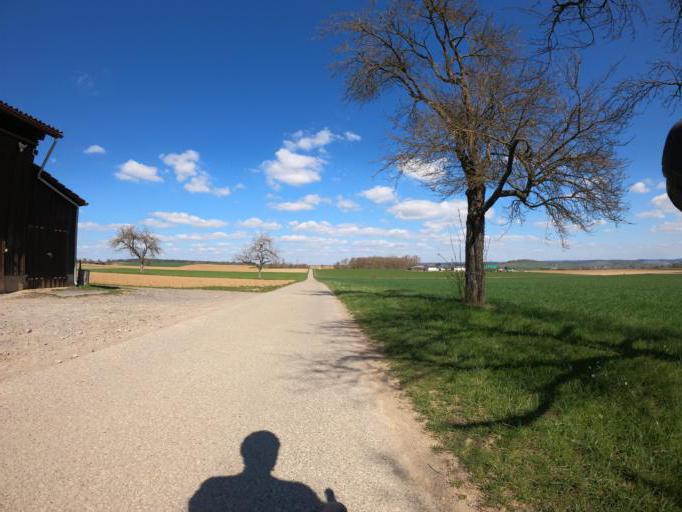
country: DE
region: Baden-Wuerttemberg
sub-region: Tuebingen Region
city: Rottenburg
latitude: 48.4686
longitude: 8.8871
